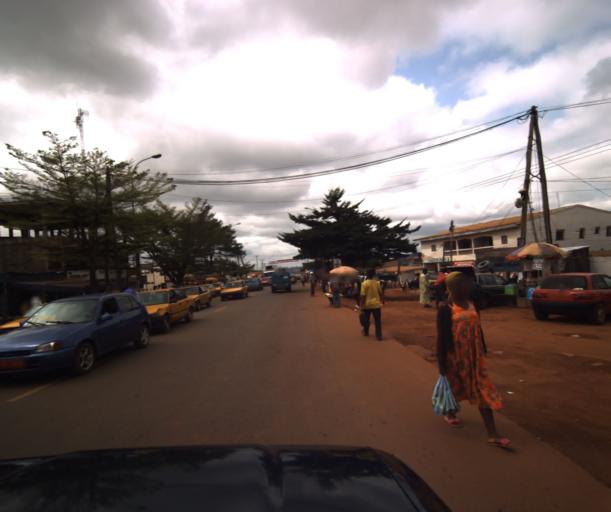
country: CM
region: Centre
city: Yaounde
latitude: 3.8265
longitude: 11.5173
